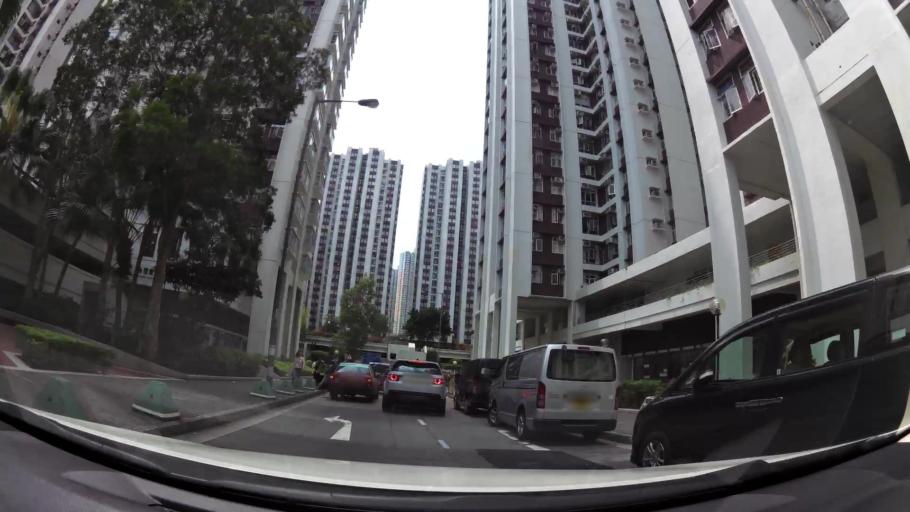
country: HK
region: Kowloon City
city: Kowloon
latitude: 22.2867
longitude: 114.2201
